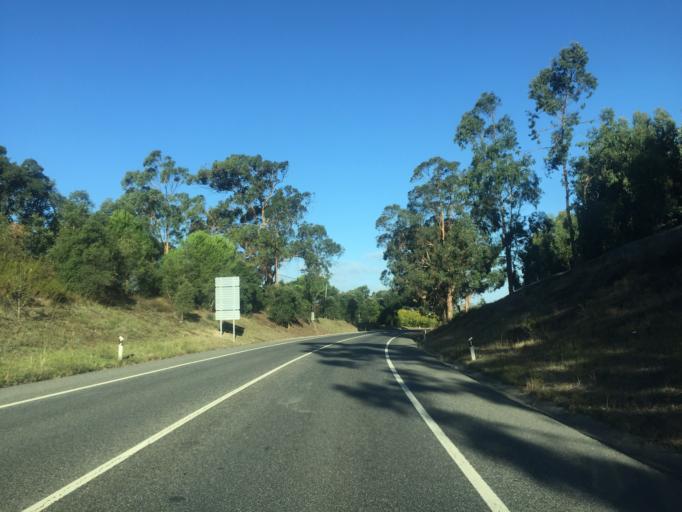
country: PT
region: Lisbon
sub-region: Azambuja
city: Alcoentre
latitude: 39.1744
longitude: -8.9352
